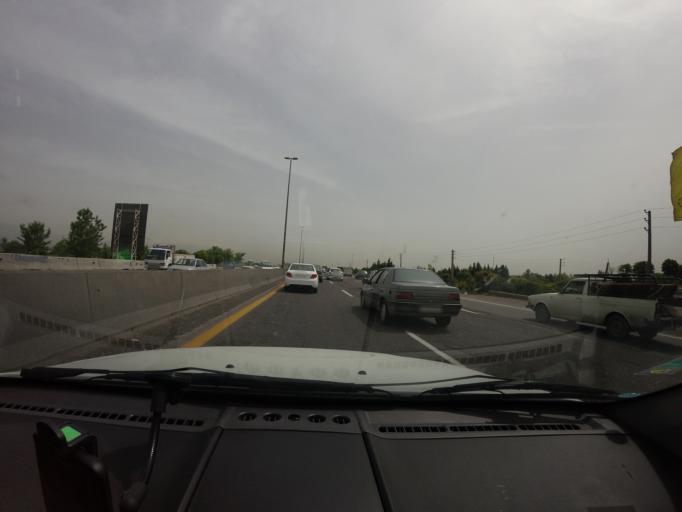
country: IR
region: Tehran
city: Eslamshahr
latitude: 35.5838
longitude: 51.1629
